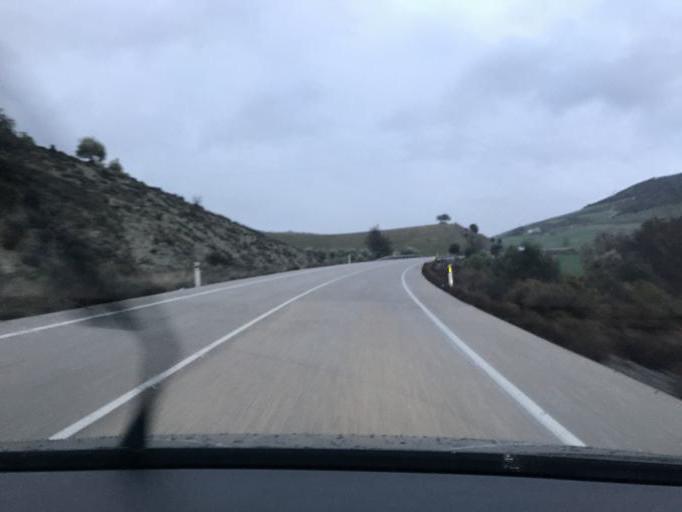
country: ES
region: Andalusia
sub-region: Provincia de Granada
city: Campotejar
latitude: 37.4644
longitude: -3.5988
